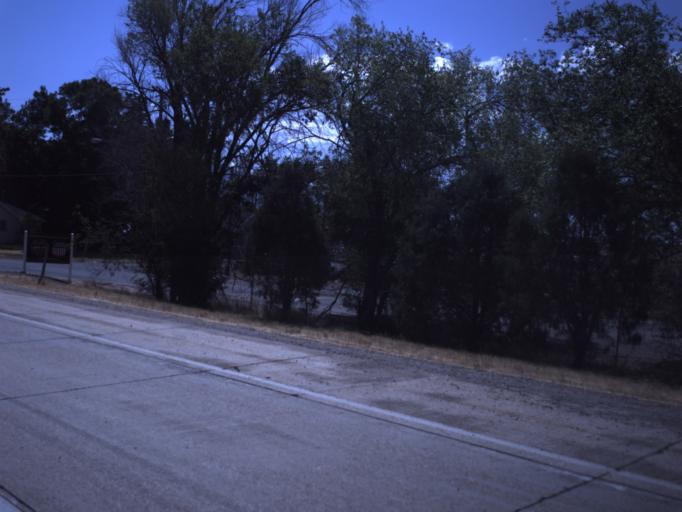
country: US
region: Utah
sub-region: Weber County
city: Ogden
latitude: 41.2295
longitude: -111.9842
